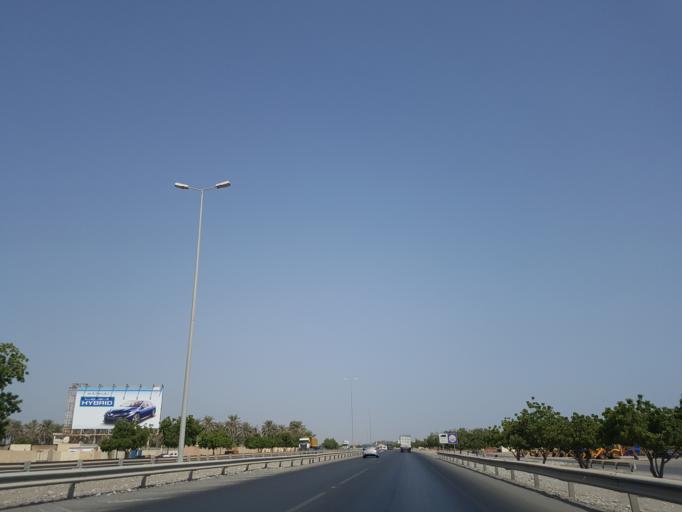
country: OM
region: Al Batinah
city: As Suwayq
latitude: 23.7483
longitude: 57.6163
